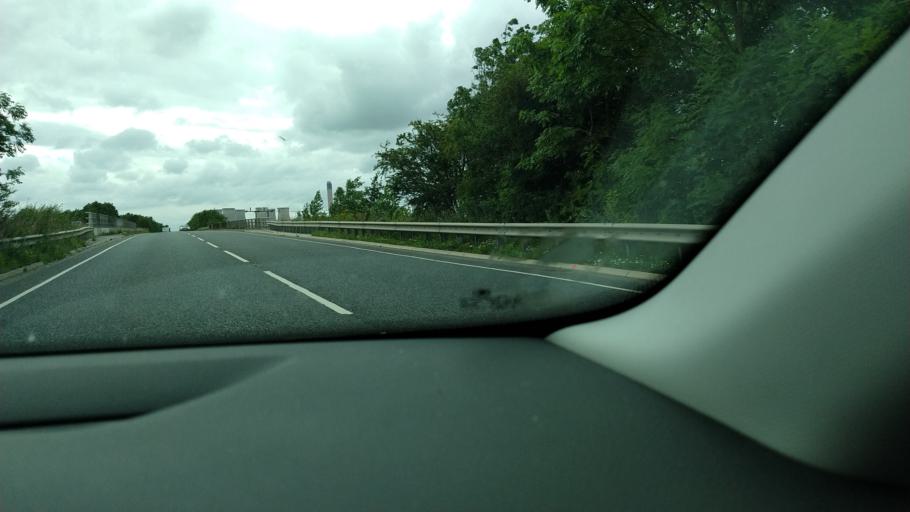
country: GB
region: England
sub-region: East Riding of Yorkshire
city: Rawcliffe
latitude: 53.7139
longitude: -0.9571
